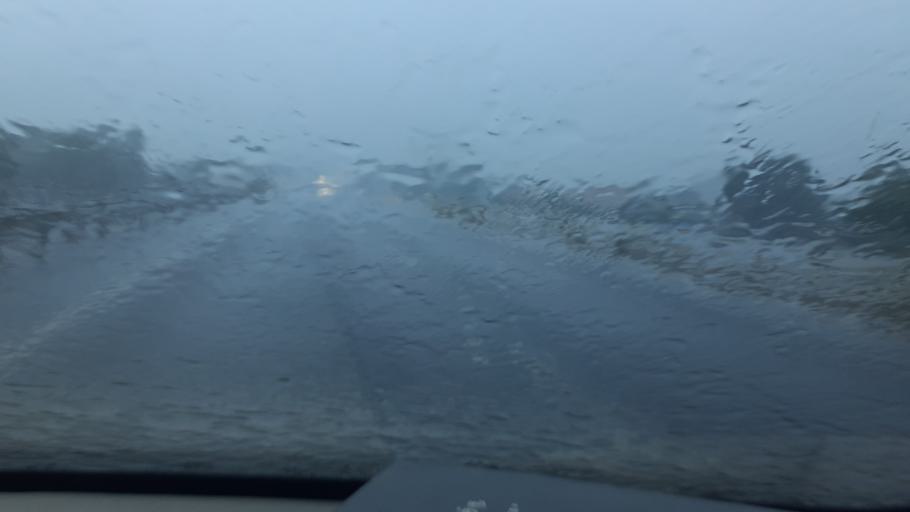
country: IN
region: Tamil Nadu
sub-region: Virudhunagar
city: Sattur
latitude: 9.4513
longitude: 77.9290
